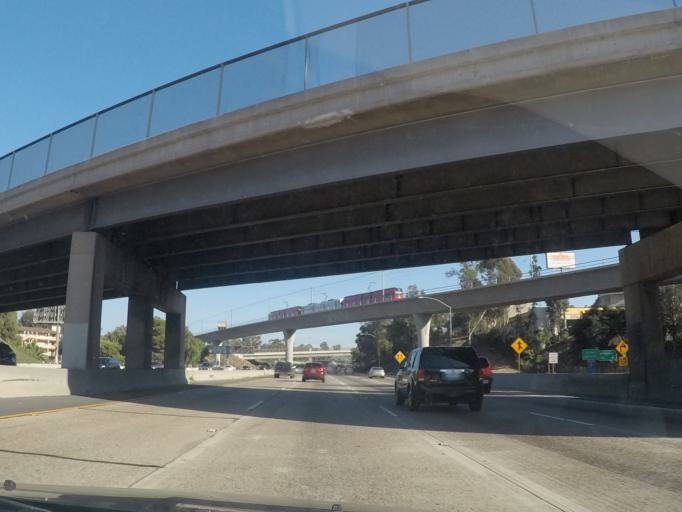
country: US
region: California
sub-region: San Diego County
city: La Mesa
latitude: 32.7734
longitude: -117.0303
